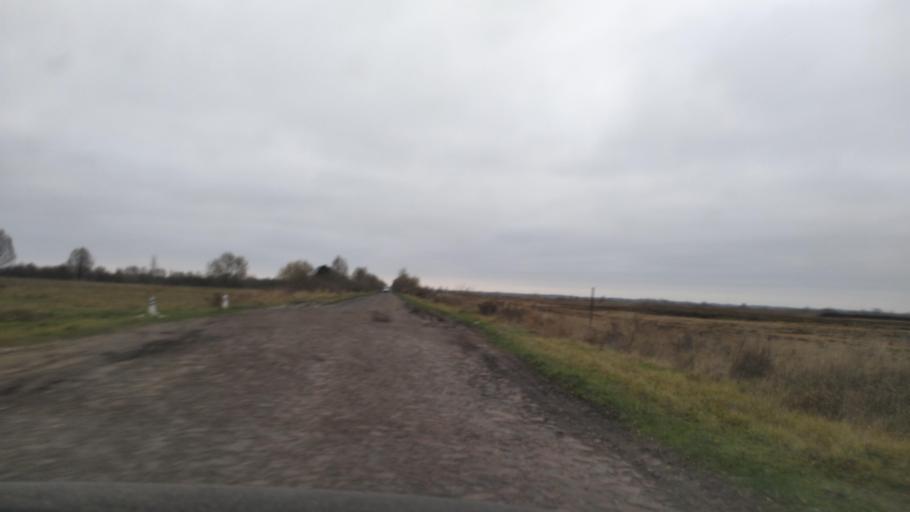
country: BY
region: Brest
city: Davyd-Haradok
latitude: 52.0046
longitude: 27.2055
